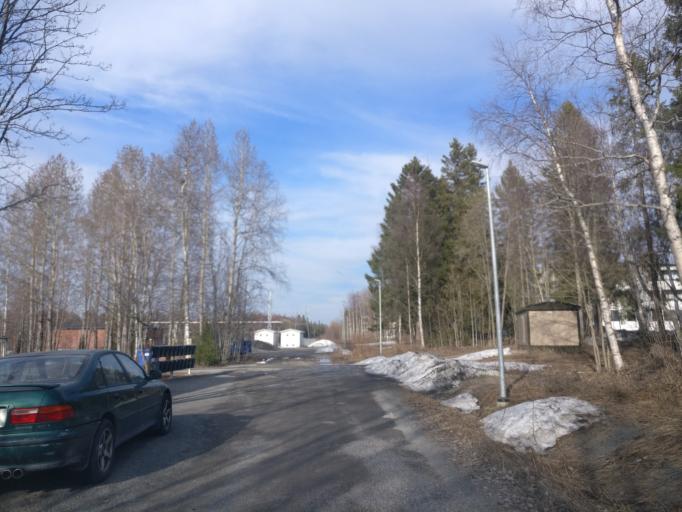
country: FI
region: Lapland
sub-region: Kemi-Tornio
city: Kemi
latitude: 65.7320
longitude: 24.5982
